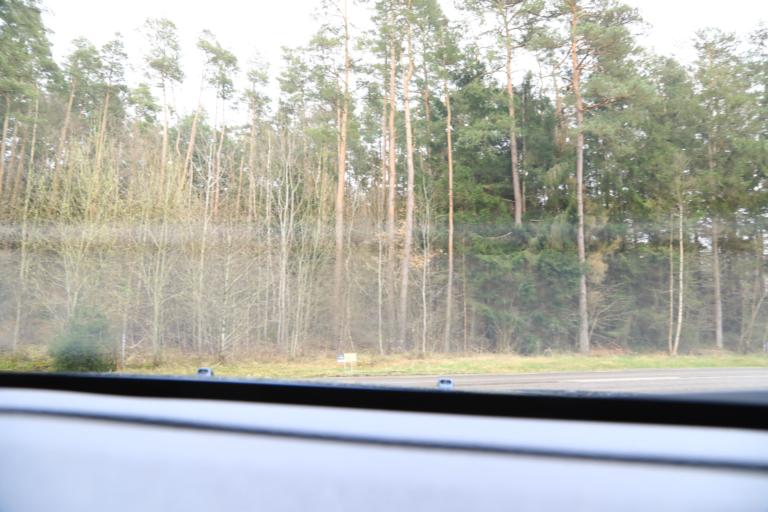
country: SE
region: Halland
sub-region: Kungsbacka Kommun
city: Frillesas
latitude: 57.3079
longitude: 12.1815
